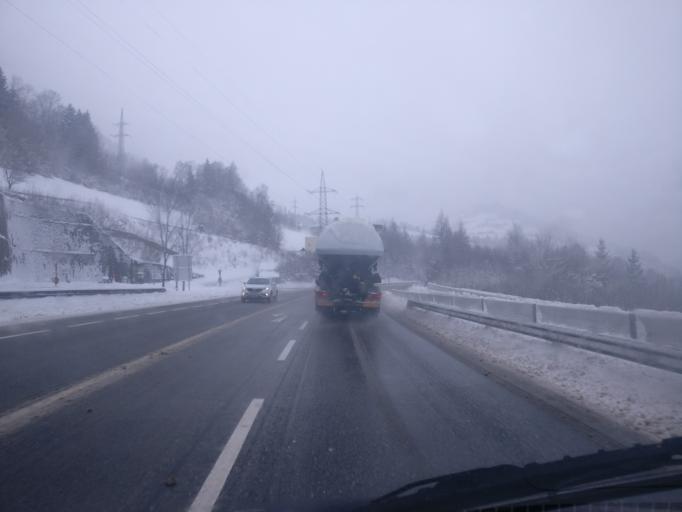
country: AT
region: Salzburg
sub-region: Politischer Bezirk Zell am See
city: Lend
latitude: 47.2941
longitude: 13.0534
